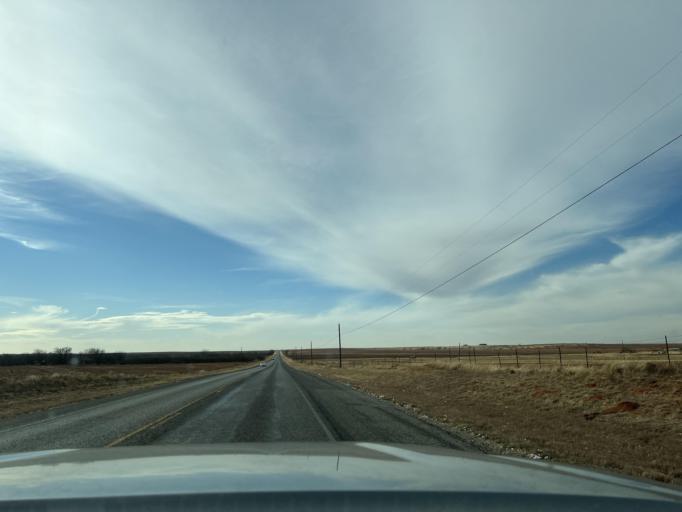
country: US
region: Texas
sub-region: Fisher County
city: Roby
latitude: 32.7412
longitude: -100.4675
